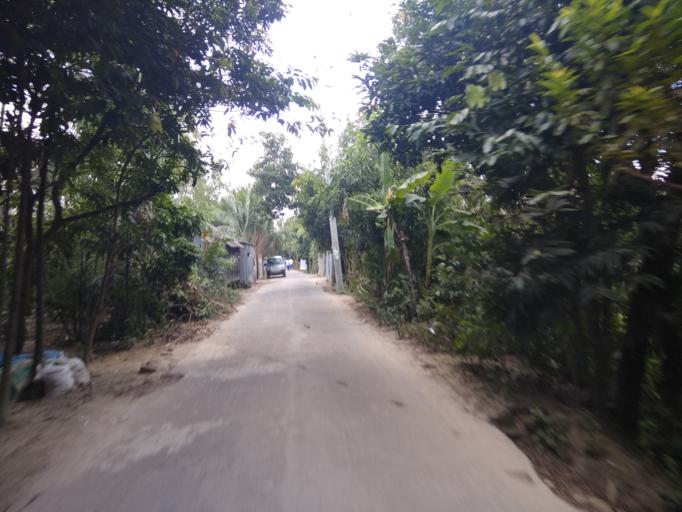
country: BD
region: Dhaka
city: Narayanganj
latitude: 23.4955
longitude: 90.4605
